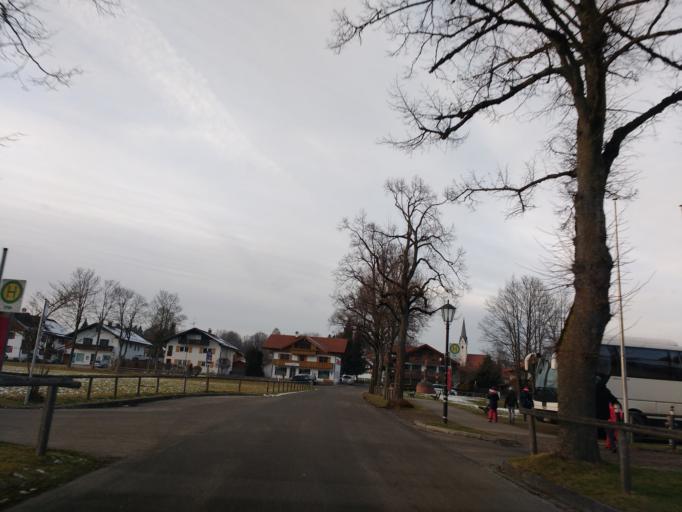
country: DE
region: Bavaria
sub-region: Swabia
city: Schwangau
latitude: 47.5741
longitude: 10.7348
